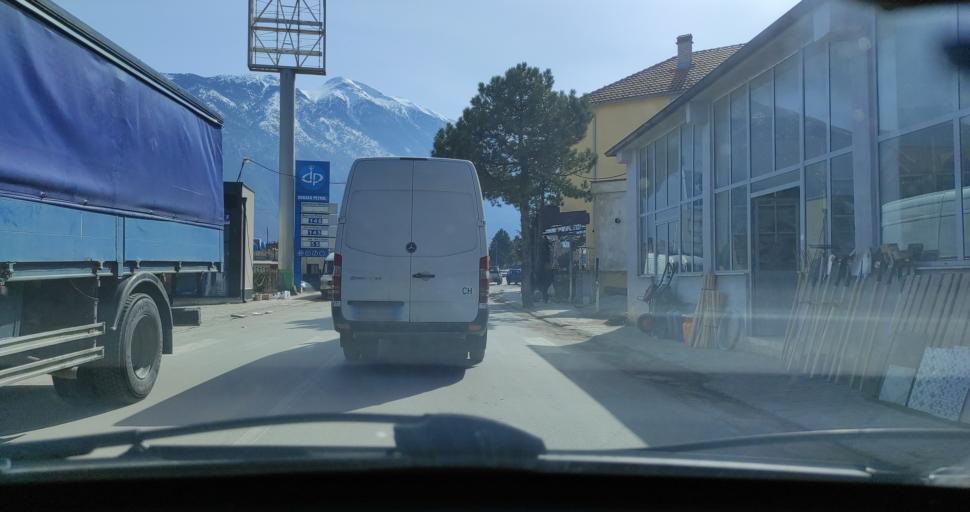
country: AL
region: Kukes
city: Kukes
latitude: 42.0764
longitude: 20.4255
